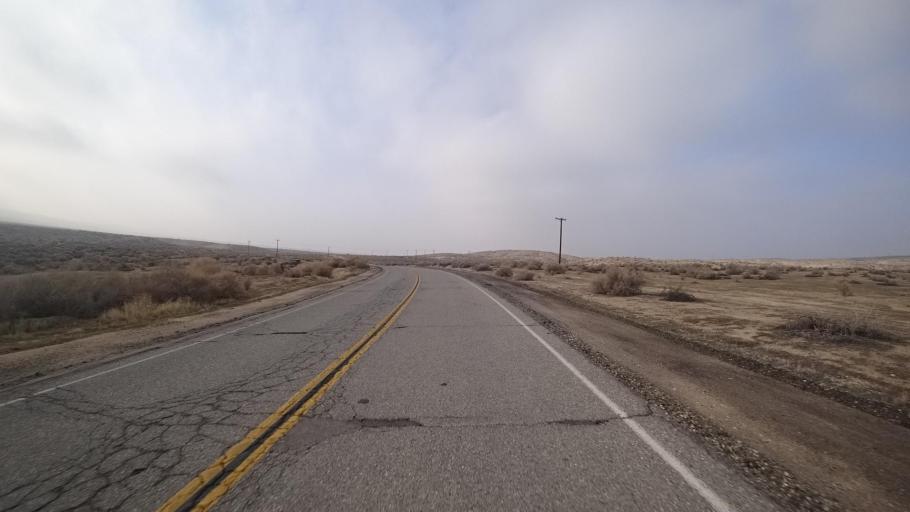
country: US
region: California
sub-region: Kern County
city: South Taft
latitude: 35.1350
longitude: -119.4070
